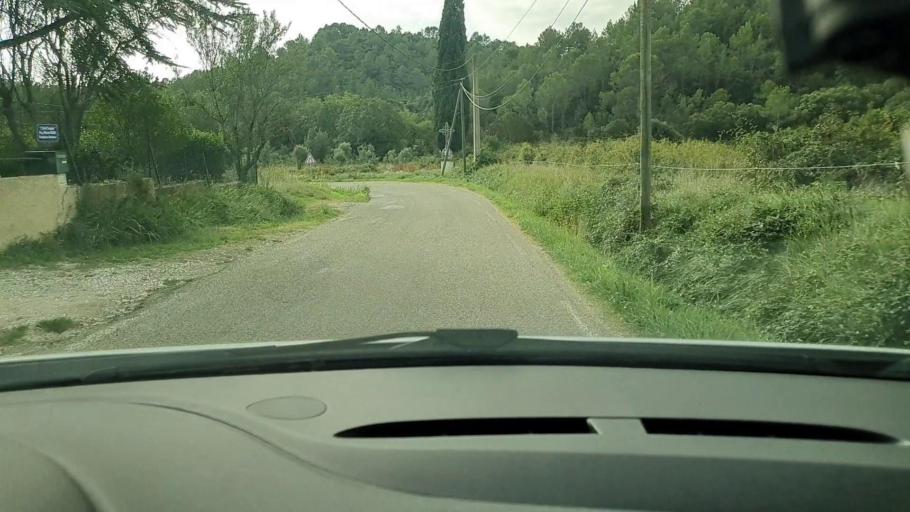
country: FR
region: Languedoc-Roussillon
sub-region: Departement du Gard
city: Montaren-et-Saint-Mediers
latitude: 44.0865
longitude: 4.3585
